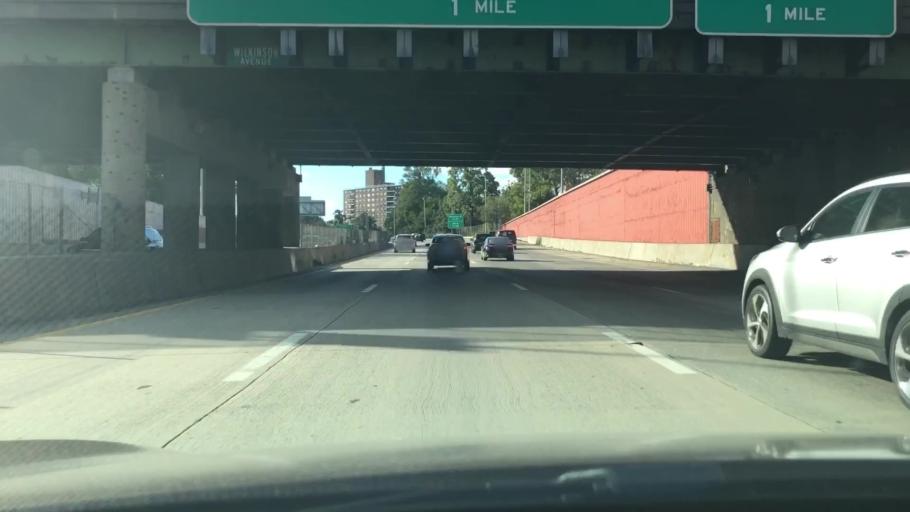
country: US
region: New York
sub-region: Bronx
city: Eastchester
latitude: 40.8519
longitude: -73.8269
